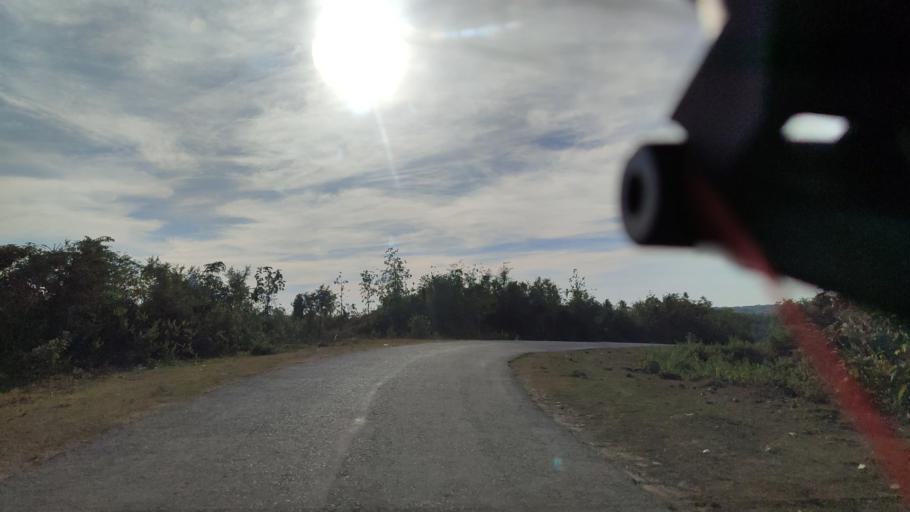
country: MM
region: Mandalay
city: Nay Pyi Taw
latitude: 19.9913
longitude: 95.8985
